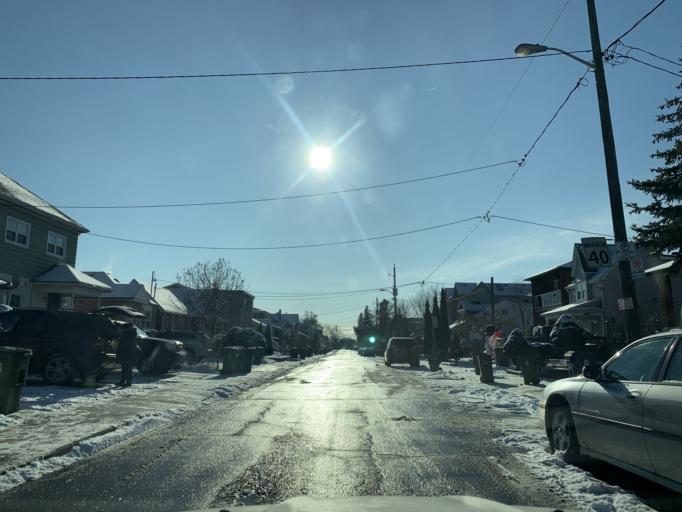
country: CA
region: Ontario
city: Toronto
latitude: 43.6817
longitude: -79.4898
